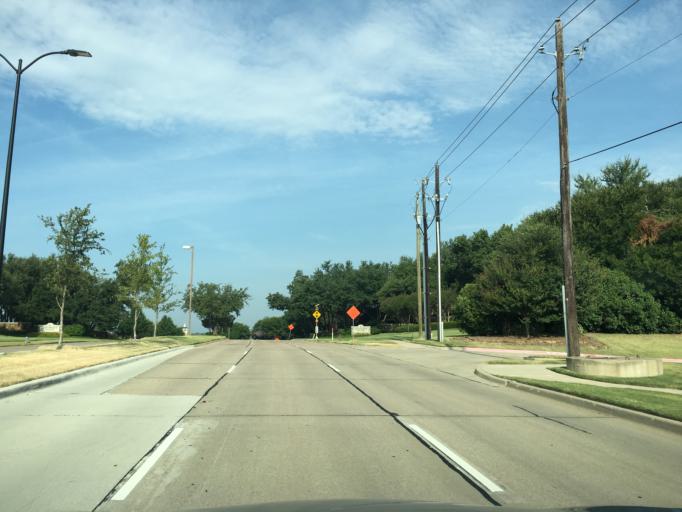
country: US
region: Texas
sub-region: Collin County
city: Fairview
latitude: 33.1988
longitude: -96.6945
